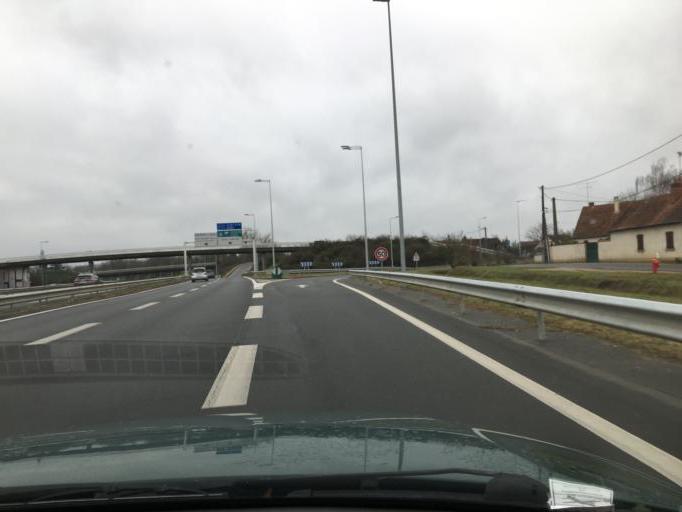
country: FR
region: Centre
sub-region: Departement du Loiret
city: Olivet
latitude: 47.8492
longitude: 1.9108
